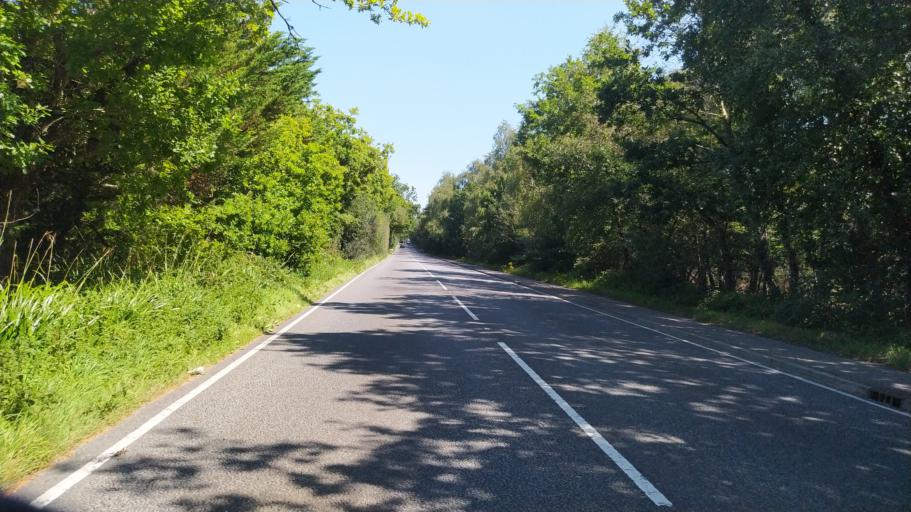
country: GB
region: England
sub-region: Dorset
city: Lytchett Matravers
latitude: 50.7248
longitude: -2.0760
